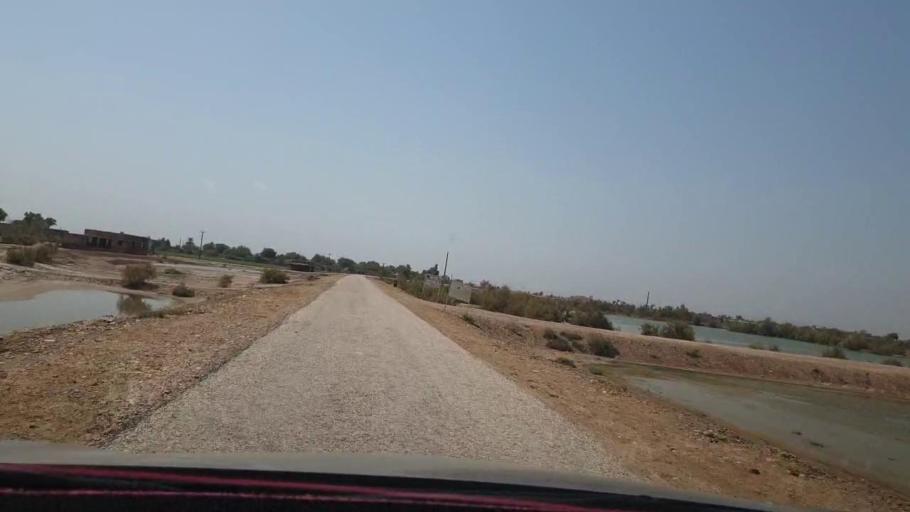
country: PK
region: Sindh
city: Warah
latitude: 27.5044
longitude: 67.7106
